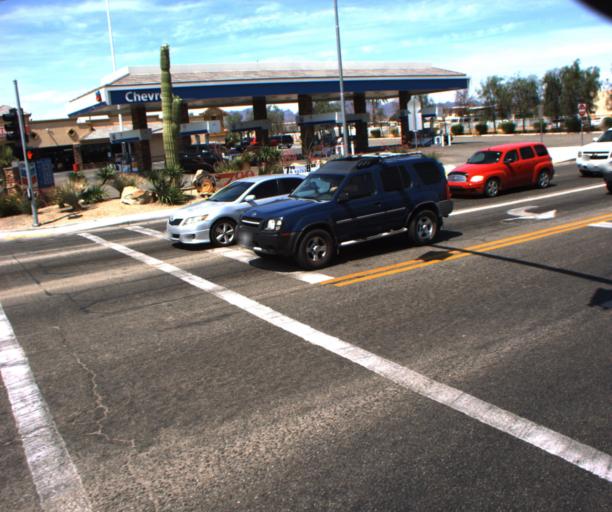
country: US
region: Arizona
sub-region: La Paz County
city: Parker
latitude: 34.1504
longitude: -114.2889
